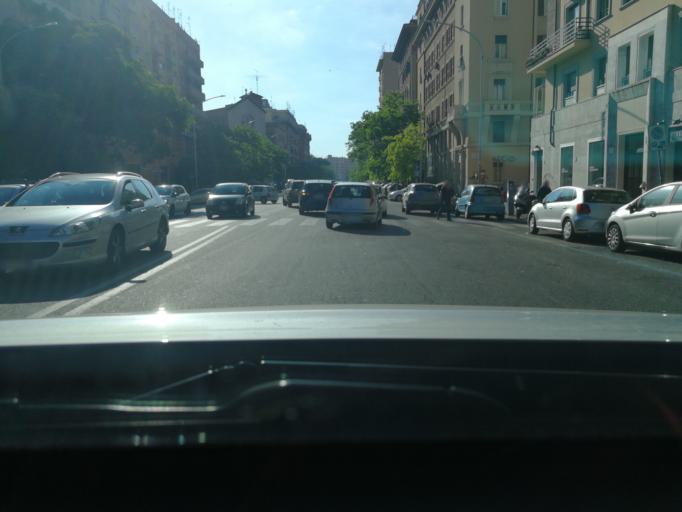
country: IT
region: Latium
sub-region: Citta metropolitana di Roma Capitale
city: Rome
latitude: 41.8849
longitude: 12.5134
